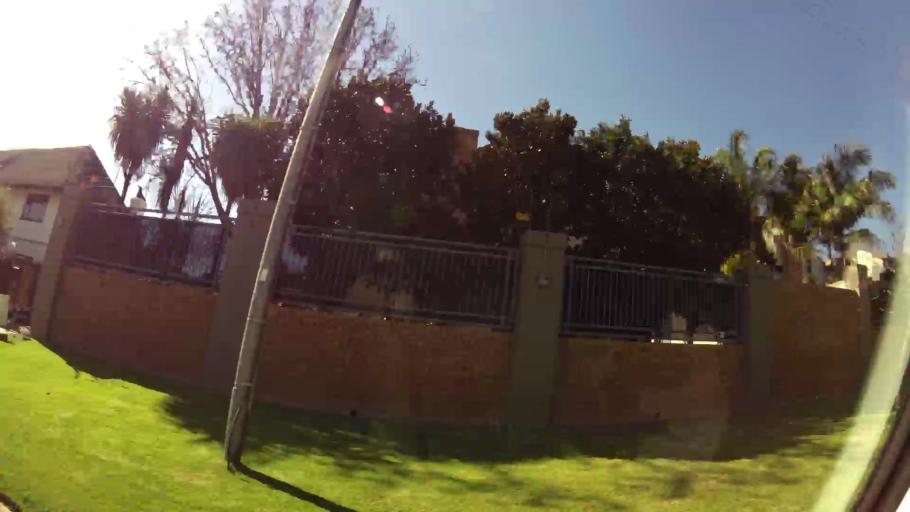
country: ZA
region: Gauteng
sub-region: City of Tshwane Metropolitan Municipality
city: Pretoria
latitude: -25.8002
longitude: 28.2412
